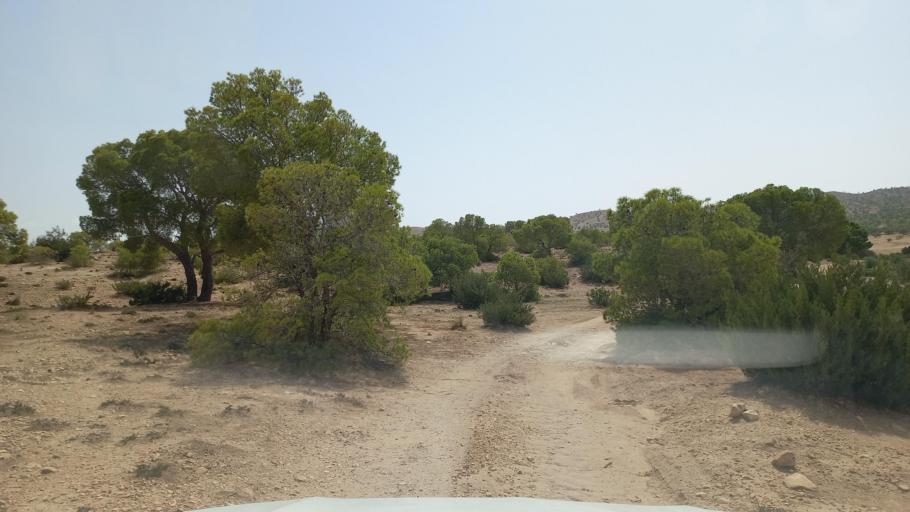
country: TN
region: Al Qasrayn
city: Sbiba
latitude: 35.3945
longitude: 8.9868
